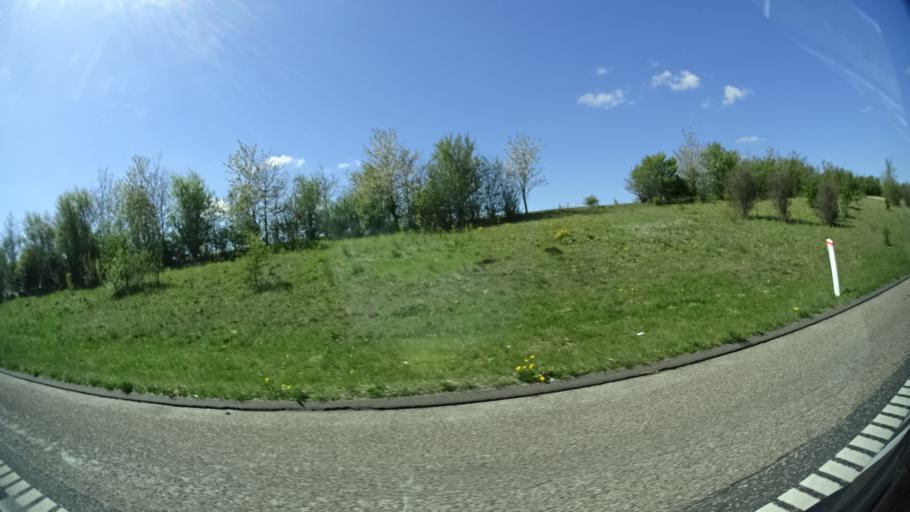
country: DK
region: Central Jutland
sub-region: Randers Kommune
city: Assentoft
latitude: 56.3715
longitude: 10.1178
